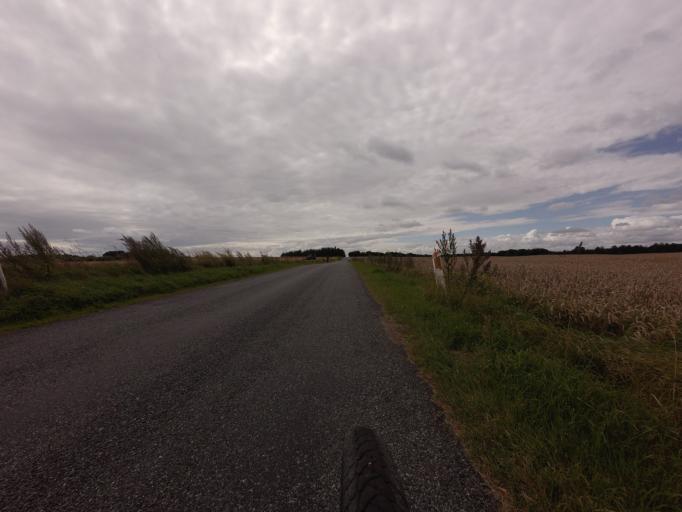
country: DK
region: Central Jutland
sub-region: Syddjurs Kommune
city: Ryomgard
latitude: 56.3859
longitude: 10.5500
